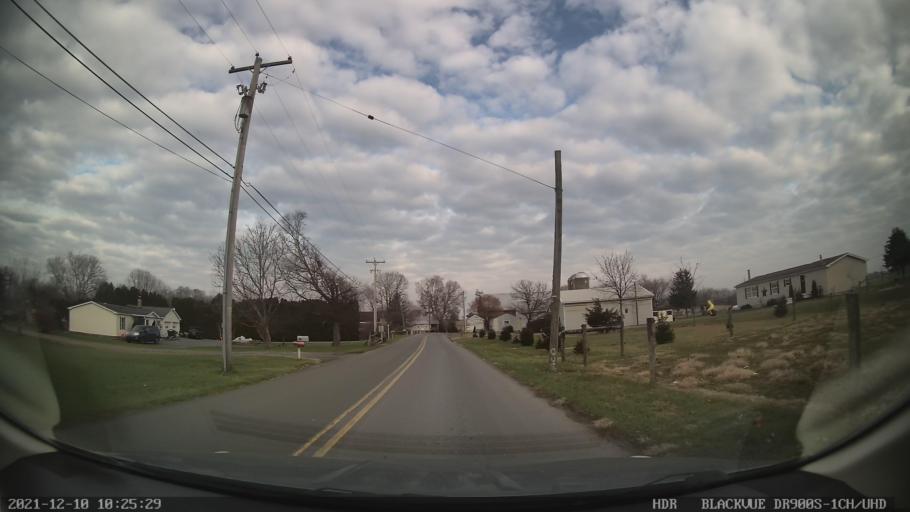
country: US
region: Pennsylvania
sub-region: Berks County
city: Topton
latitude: 40.4890
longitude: -75.7422
